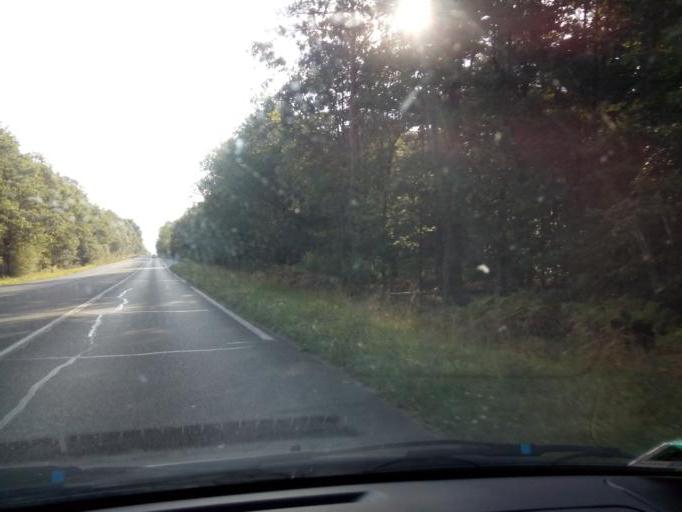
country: FR
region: Centre
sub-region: Departement d'Indre-et-Loire
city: Azay-le-Rideau
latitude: 47.2823
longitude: 0.5085
